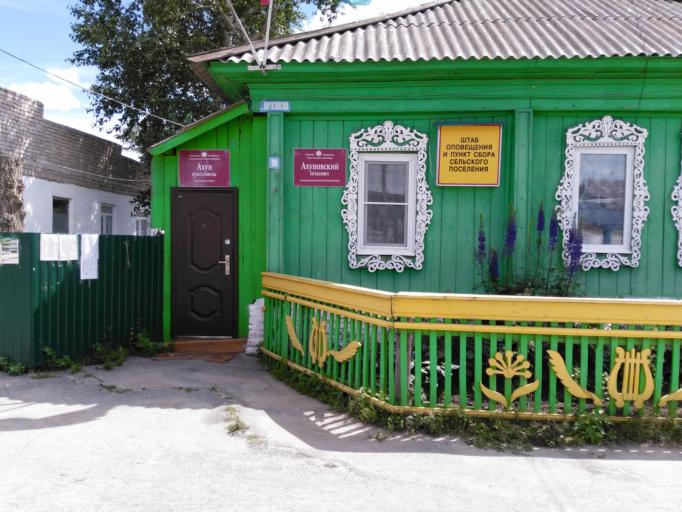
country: RU
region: Bashkortostan
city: Akhunovo
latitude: 54.2095
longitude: 59.6062
